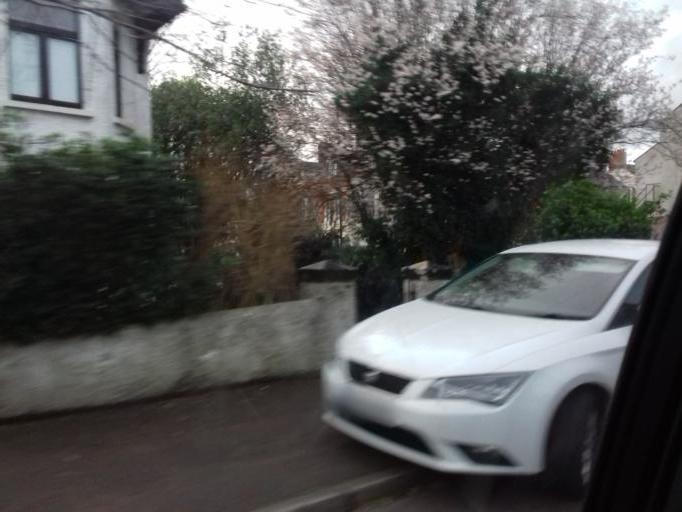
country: GB
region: Northern Ireland
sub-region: City of Belfast
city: Belfast
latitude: 54.6270
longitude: -5.9418
